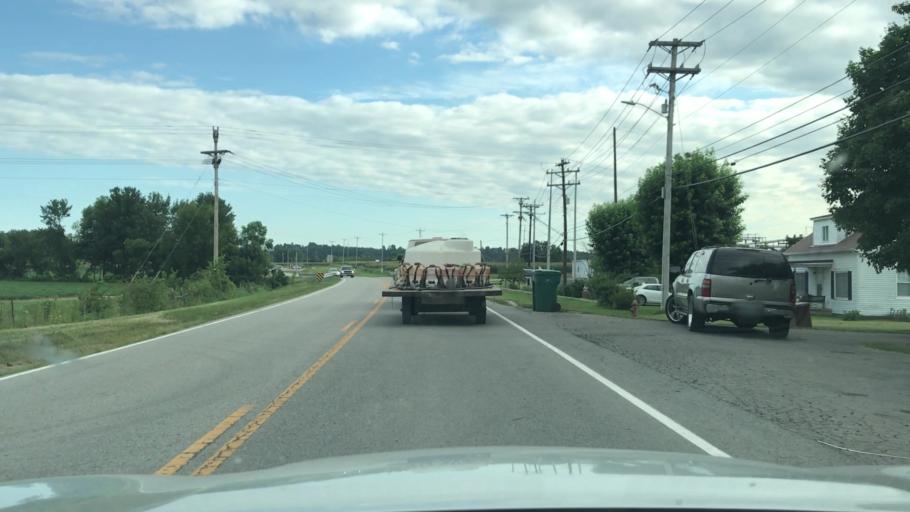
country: US
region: Kentucky
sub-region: Todd County
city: Elkton
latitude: 36.8198
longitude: -87.1512
